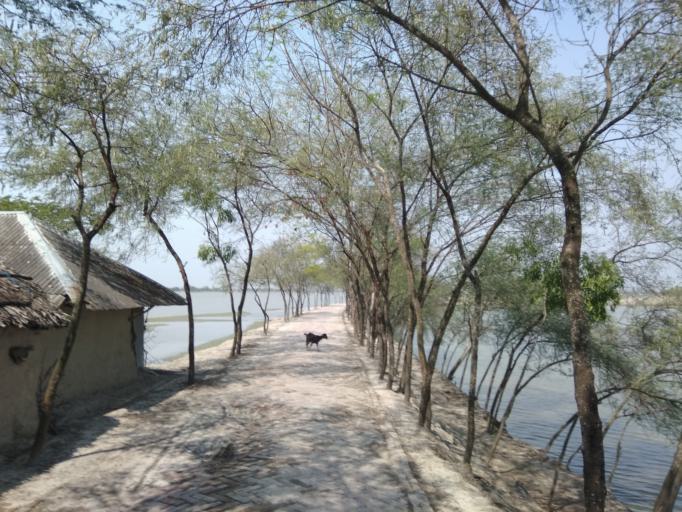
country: IN
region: West Bengal
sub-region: North 24 Parganas
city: Taki
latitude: 22.3942
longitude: 89.1918
